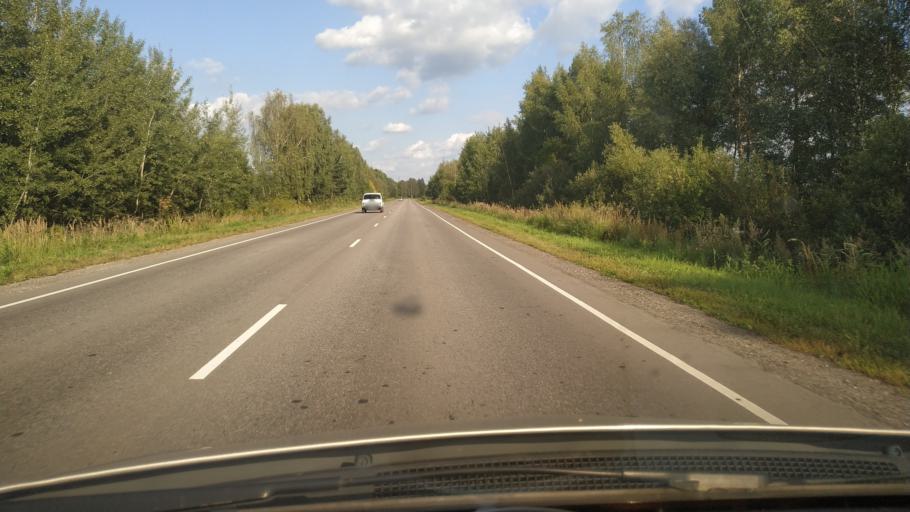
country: RU
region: Moskovskaya
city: Vereya
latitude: 55.7075
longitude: 39.1362
